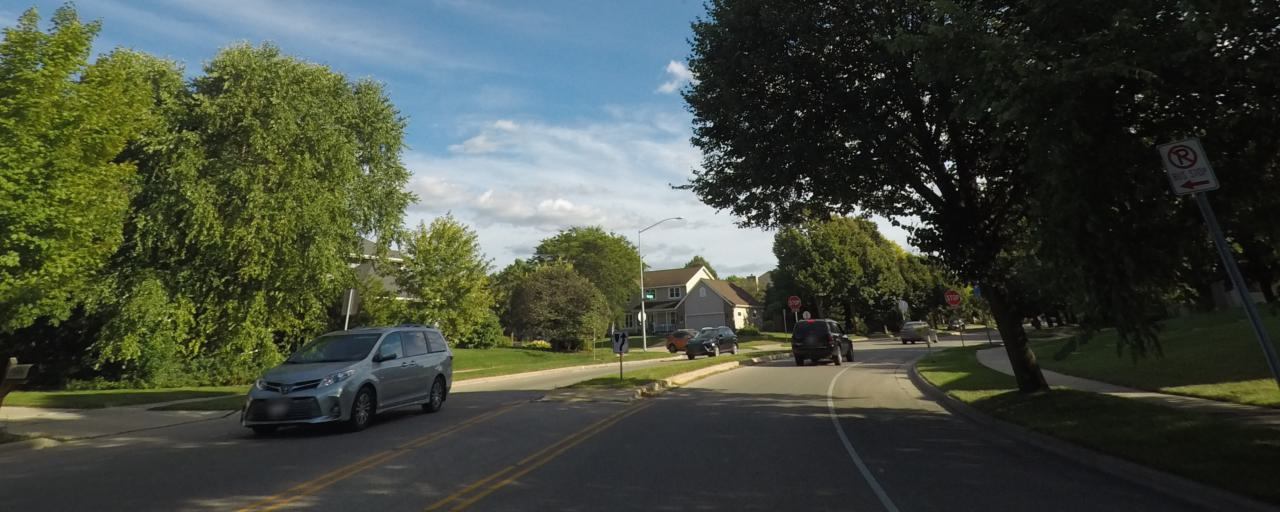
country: US
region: Wisconsin
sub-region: Dane County
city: Middleton
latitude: 43.0688
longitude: -89.5178
